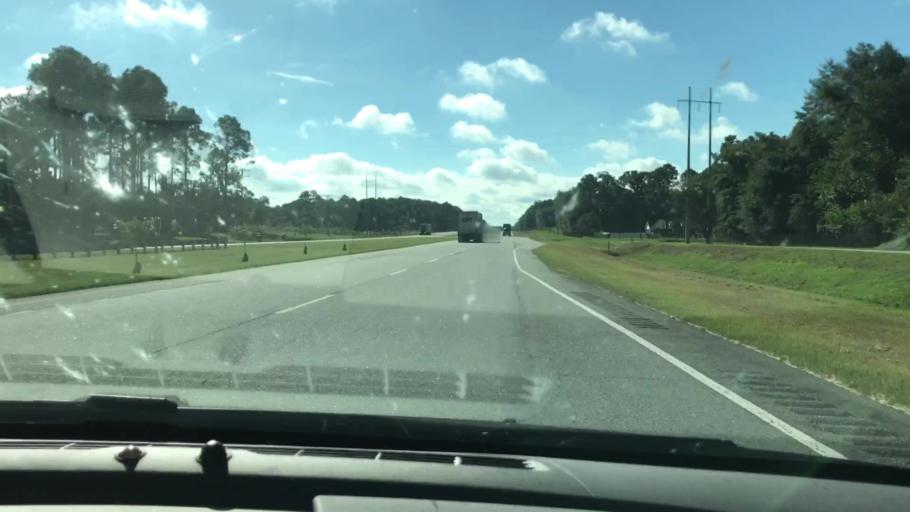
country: US
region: Georgia
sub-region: Dougherty County
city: Albany
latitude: 31.5701
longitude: -84.0248
